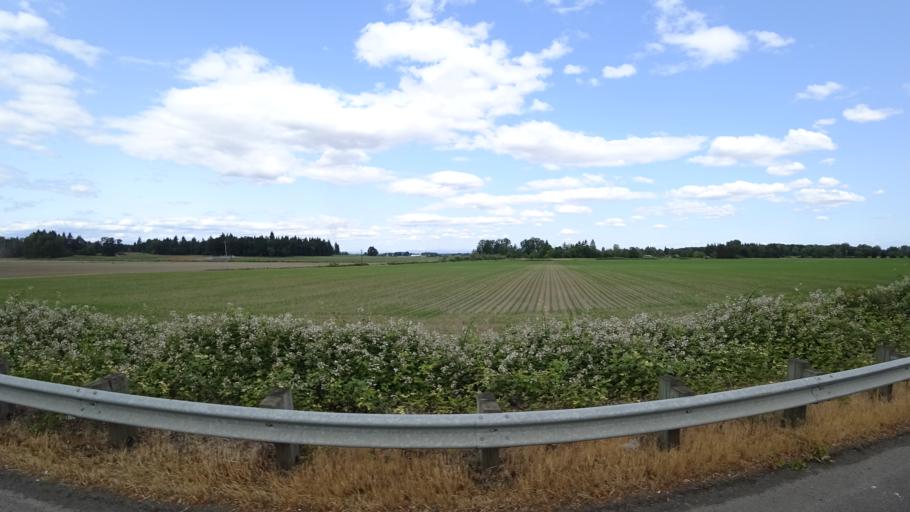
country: US
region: Oregon
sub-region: Washington County
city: Bethany
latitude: 45.6311
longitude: -122.8166
